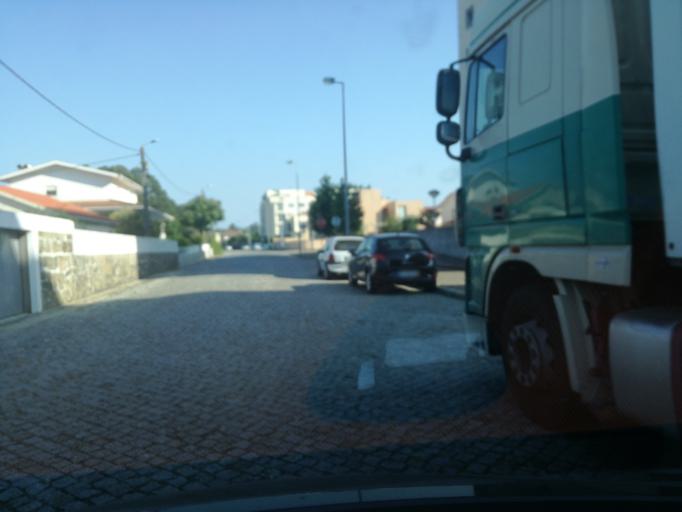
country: PT
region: Porto
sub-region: Maia
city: Gemunde
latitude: 41.2614
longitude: -8.6638
